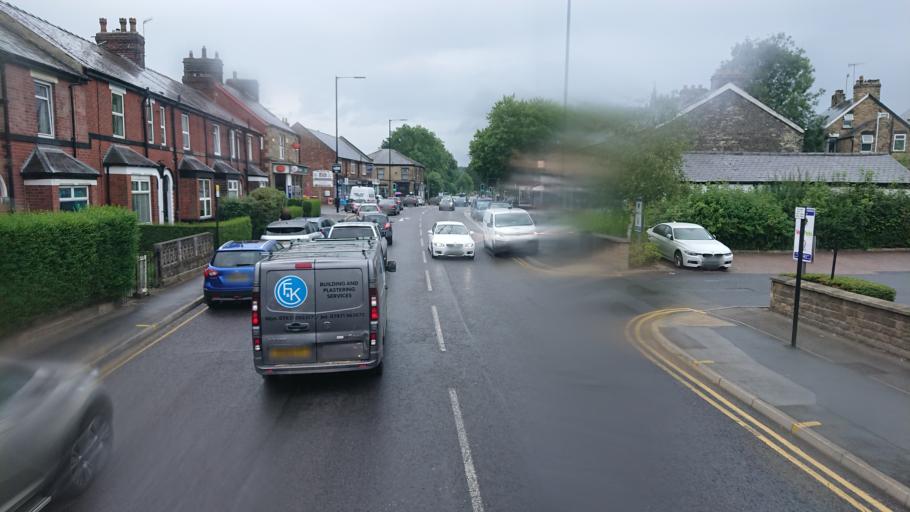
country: GB
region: England
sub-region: Sheffield
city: Sheffield
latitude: 53.3467
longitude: -1.4959
